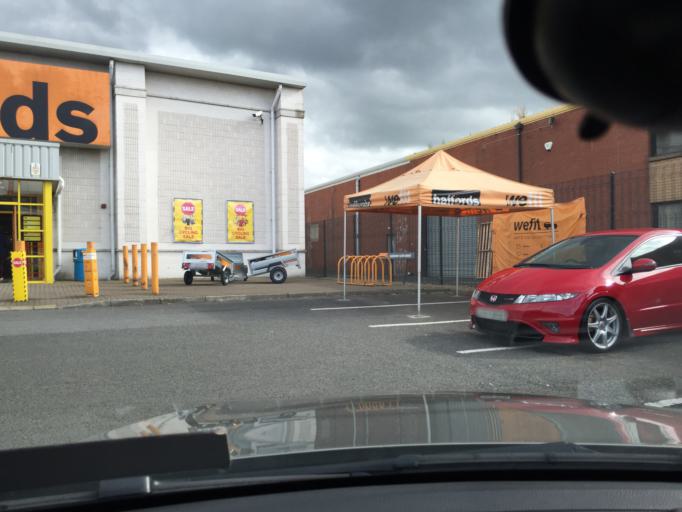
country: GB
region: Northern Ireland
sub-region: City of Belfast
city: Belfast
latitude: 54.5776
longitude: -5.9623
